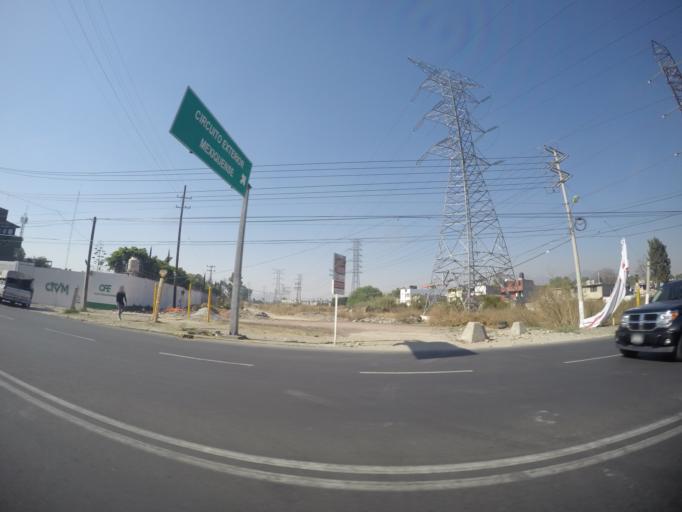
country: MX
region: Mexico
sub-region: Atenco
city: Colonia el Salado
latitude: 19.5892
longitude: -99.0266
